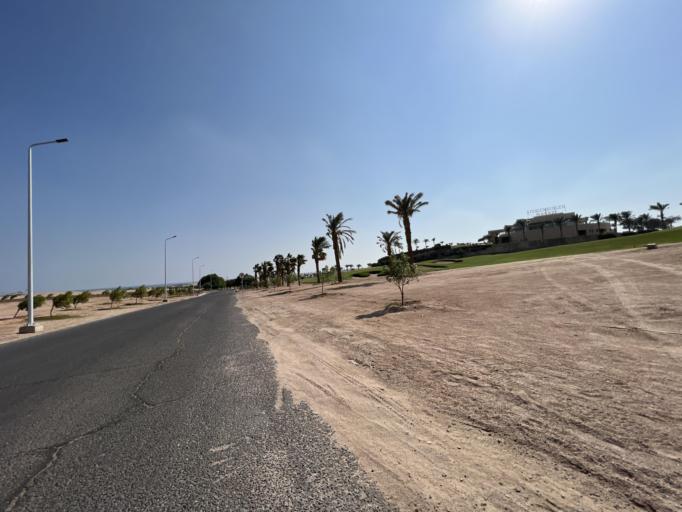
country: EG
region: Red Sea
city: Makadi Bay
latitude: 26.9856
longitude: 33.8865
